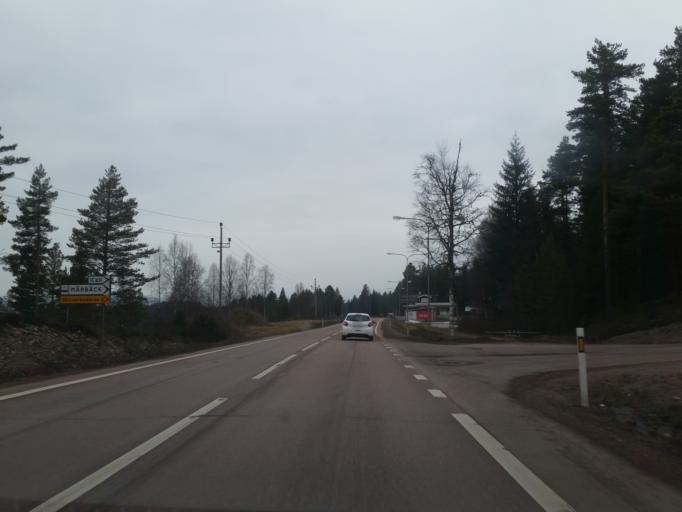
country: SE
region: Dalarna
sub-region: Alvdalens Kommun
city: AElvdalen
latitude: 61.1999
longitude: 14.0746
